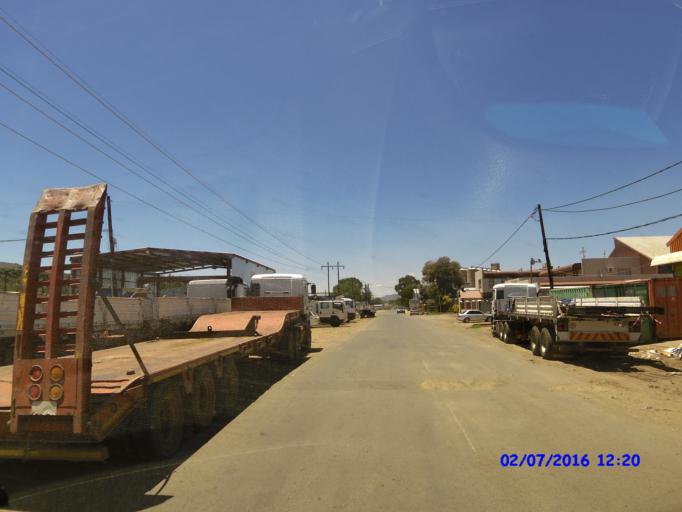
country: LS
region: Maseru
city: Maseru
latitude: -29.2961
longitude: 27.4744
